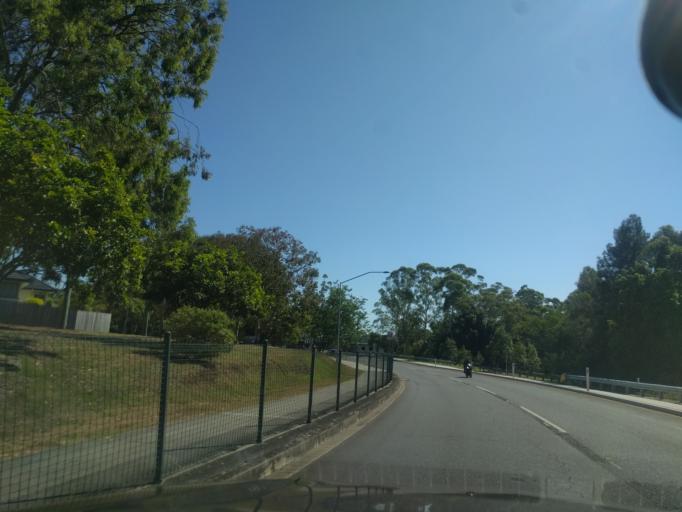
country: AU
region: Queensland
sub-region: Brisbane
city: Stafford
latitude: -27.4134
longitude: 153.0062
